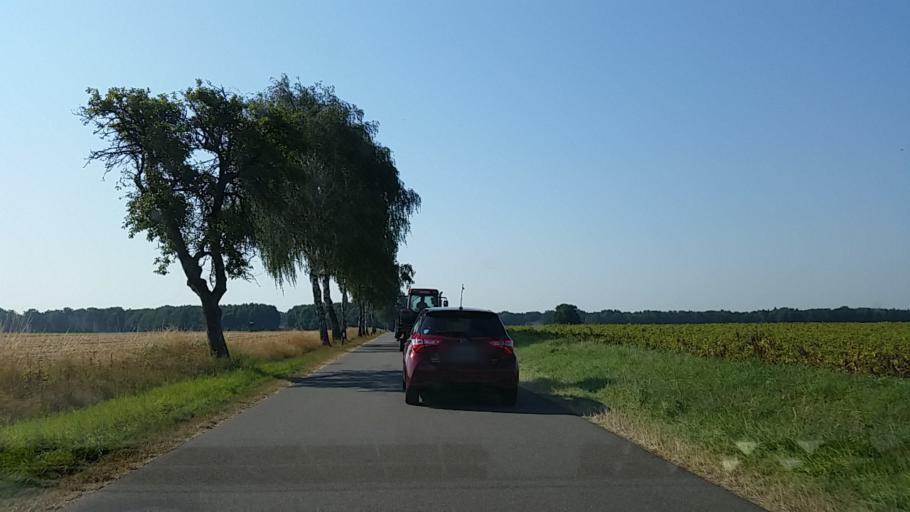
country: DE
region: Lower Saxony
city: Luder
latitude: 52.8186
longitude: 10.6299
